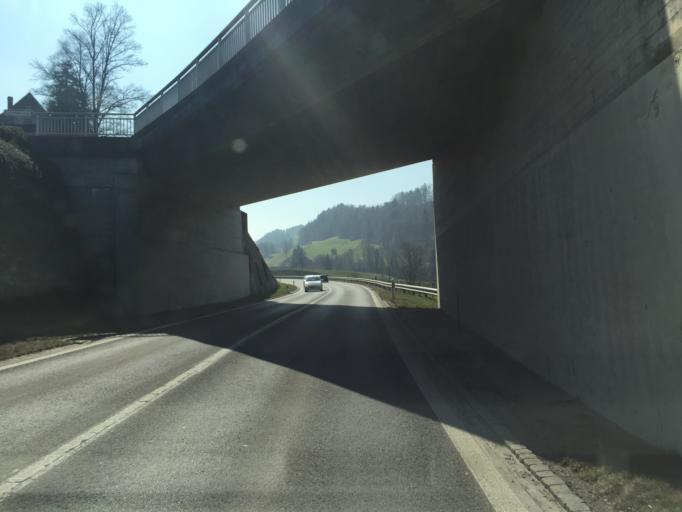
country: CH
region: Saint Gallen
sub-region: Wahlkreis Toggenburg
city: Lichtensteig
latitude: 47.3416
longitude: 9.0819
